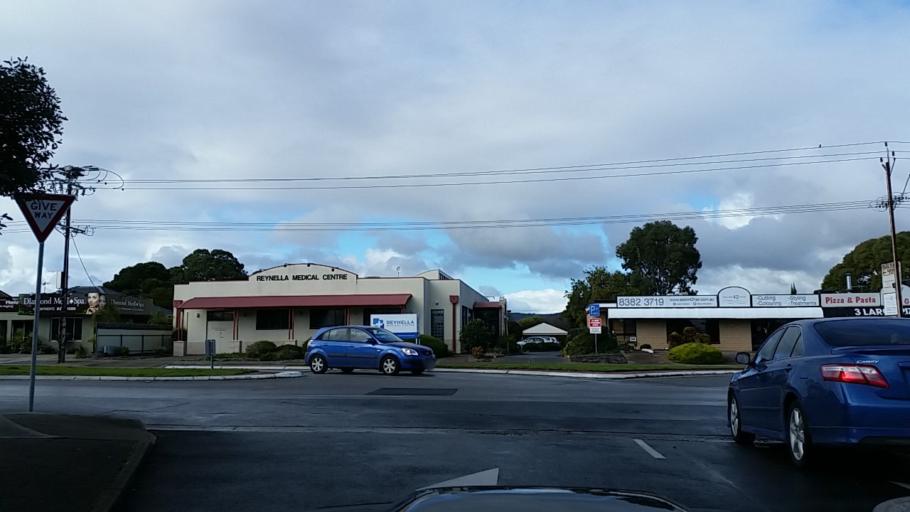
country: AU
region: South Australia
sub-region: Onkaparinga
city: Reynella
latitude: -35.1064
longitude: 138.5219
